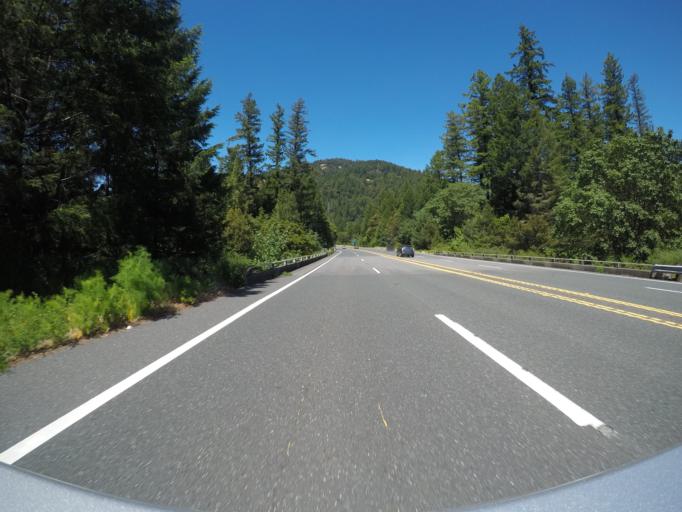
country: US
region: California
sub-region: Humboldt County
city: Redway
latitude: 39.9519
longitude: -123.7806
